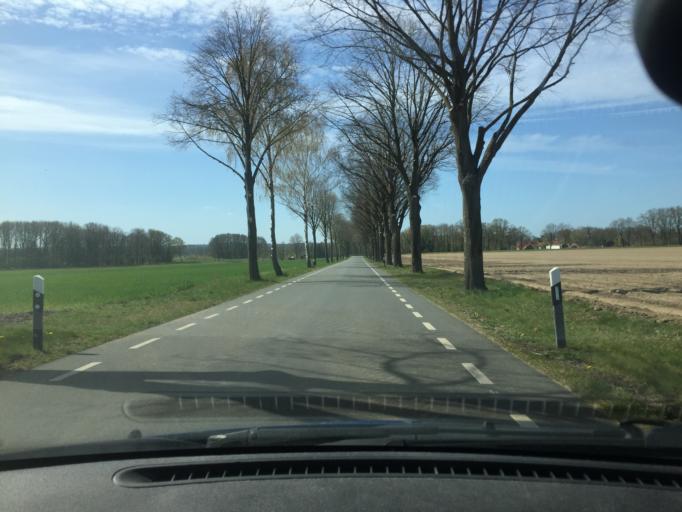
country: DE
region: Lower Saxony
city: Wieren
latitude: 52.9126
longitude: 10.6778
